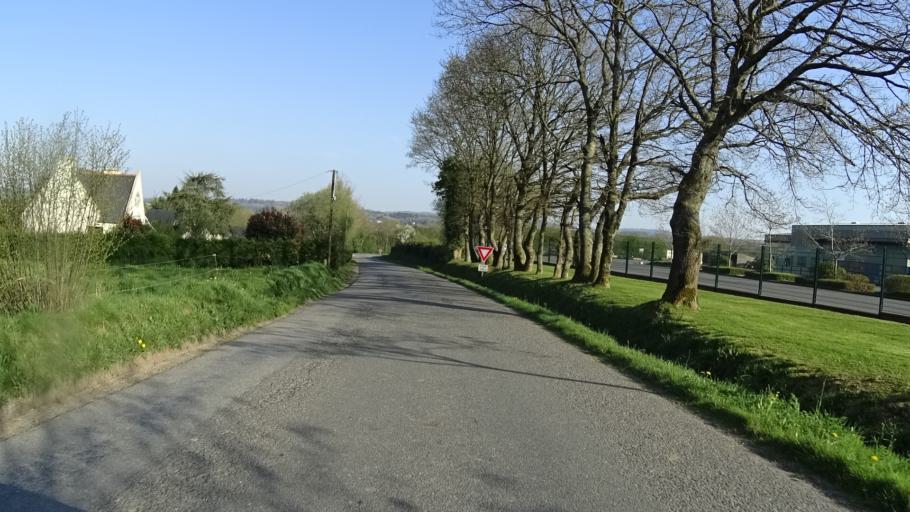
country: FR
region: Brittany
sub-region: Departement du Finistere
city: Sizun
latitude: 48.3994
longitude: -4.0836
